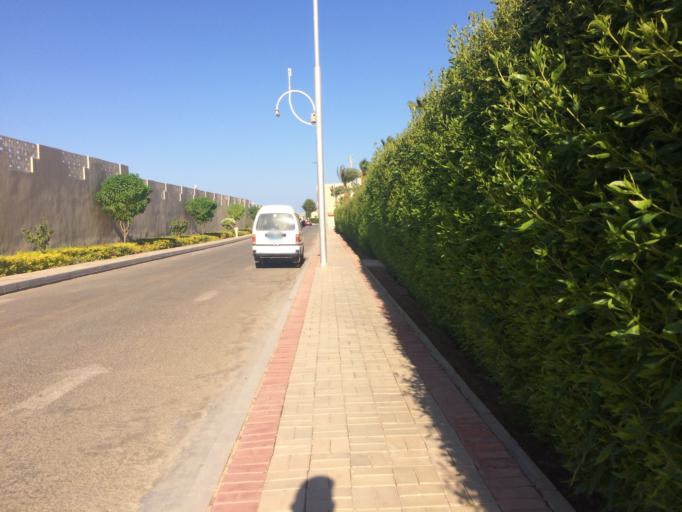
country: EG
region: Red Sea
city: Hurghada
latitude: 27.1231
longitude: 33.8266
